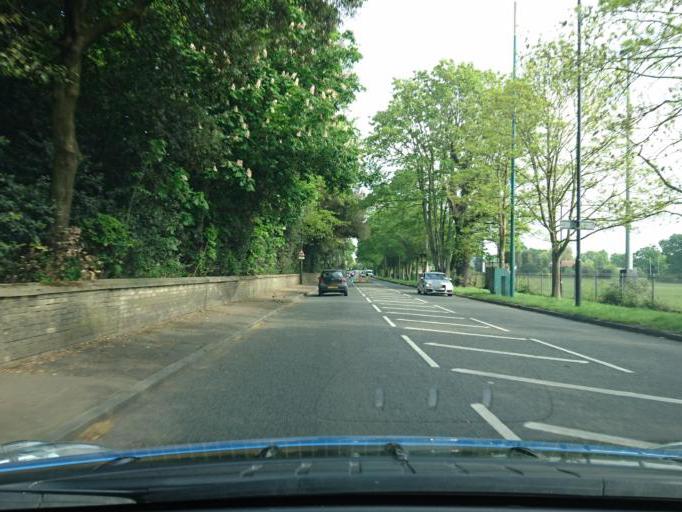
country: GB
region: England
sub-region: Greater London
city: Hadley Wood
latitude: 51.6415
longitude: -0.1442
